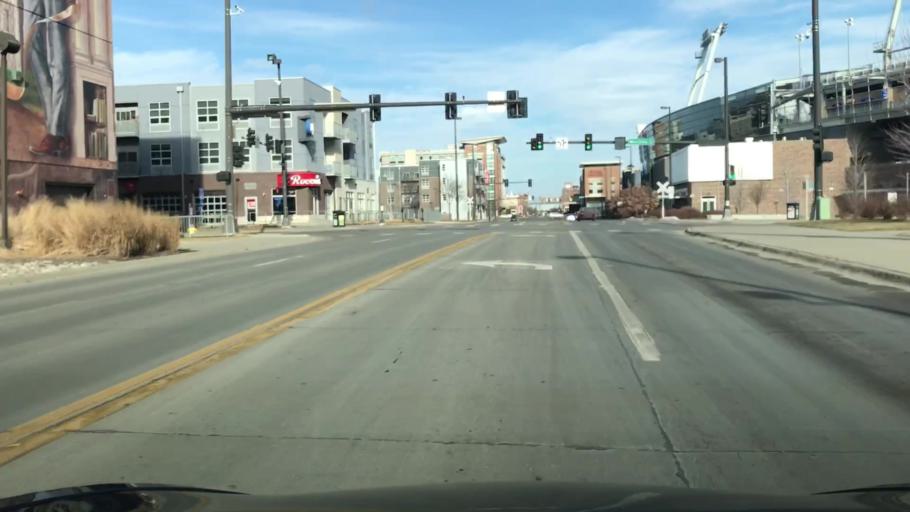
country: US
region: Nebraska
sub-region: Douglas County
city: Omaha
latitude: 41.2653
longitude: -95.9331
